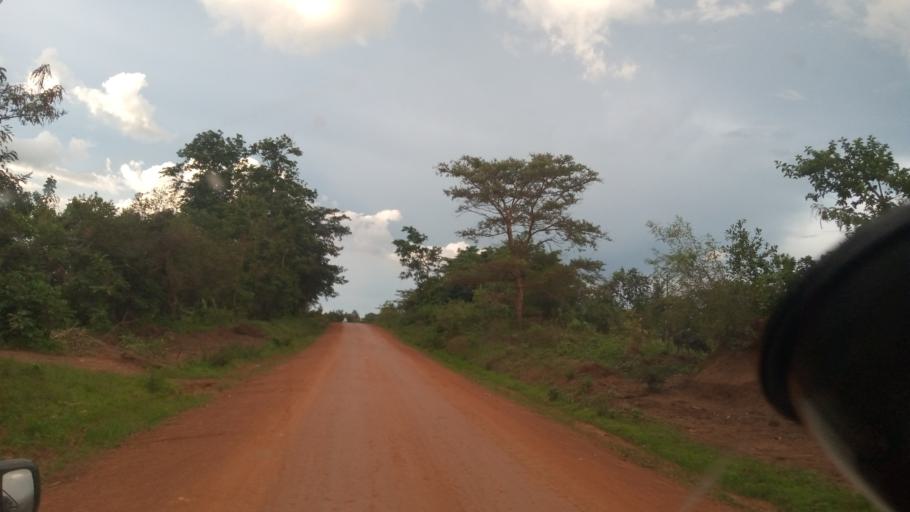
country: UG
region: Northern Region
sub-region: Kole District
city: Kole
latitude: 2.3902
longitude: 32.9334
